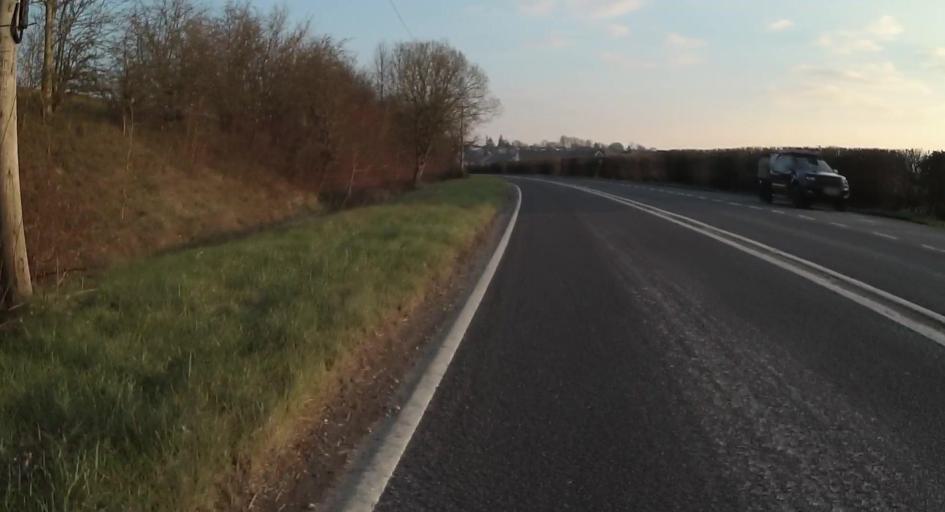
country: GB
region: England
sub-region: Hampshire
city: Alton
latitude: 51.1536
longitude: -0.9892
